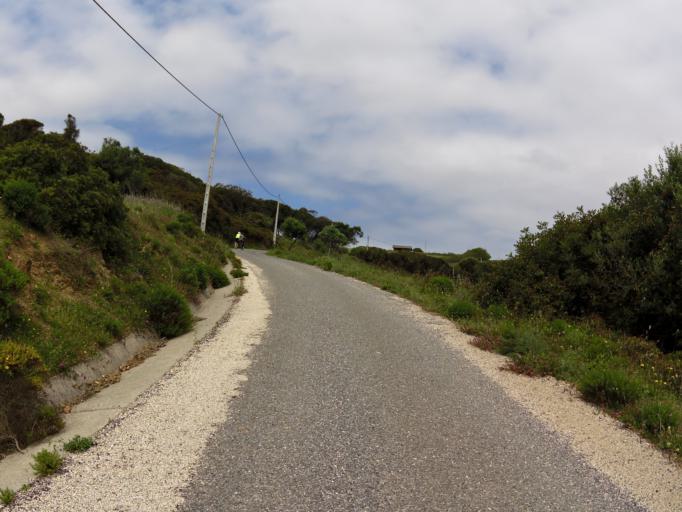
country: PT
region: Faro
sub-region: Vila do Bispo
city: Vila do Bispo
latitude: 37.0774
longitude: -8.8766
